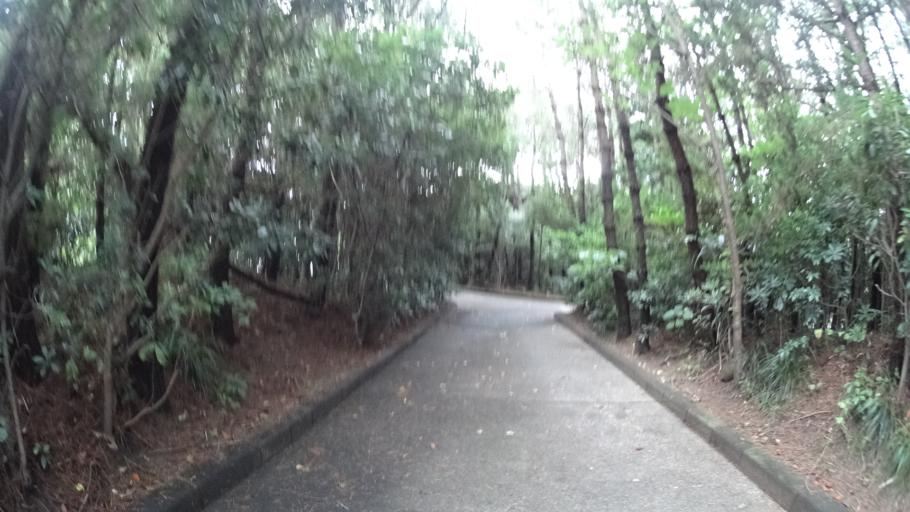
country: JP
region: Shizuoka
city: Shimoda
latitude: 34.3329
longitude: 139.2104
